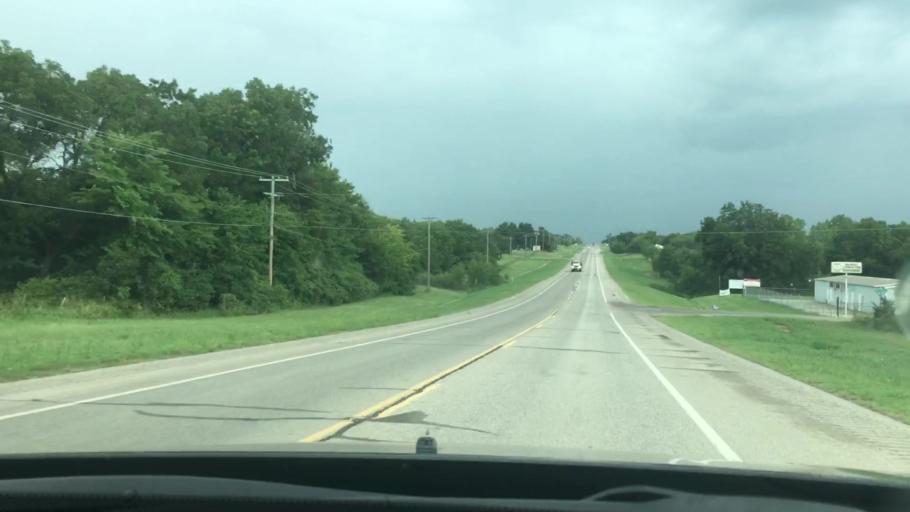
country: US
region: Oklahoma
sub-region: Carter County
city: Healdton
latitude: 34.2049
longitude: -97.4748
